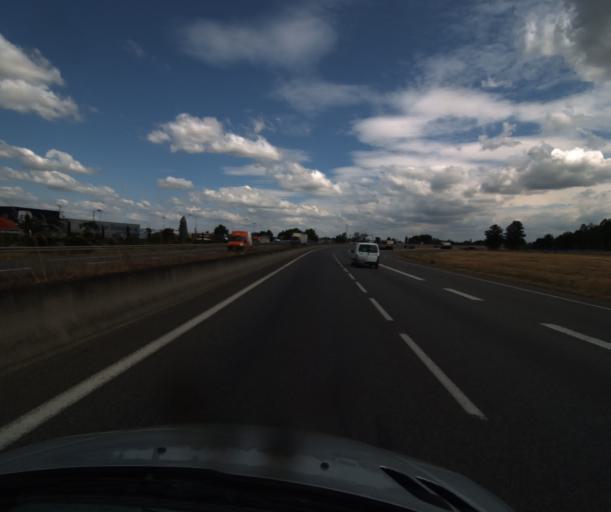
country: FR
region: Midi-Pyrenees
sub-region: Departement du Tarn-et-Garonne
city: Bressols
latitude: 43.9867
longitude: 1.3356
